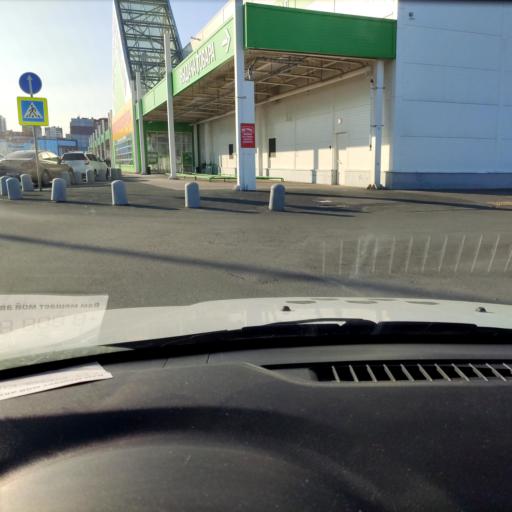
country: RU
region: Samara
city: Tol'yatti
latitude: 53.5508
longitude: 49.3400
